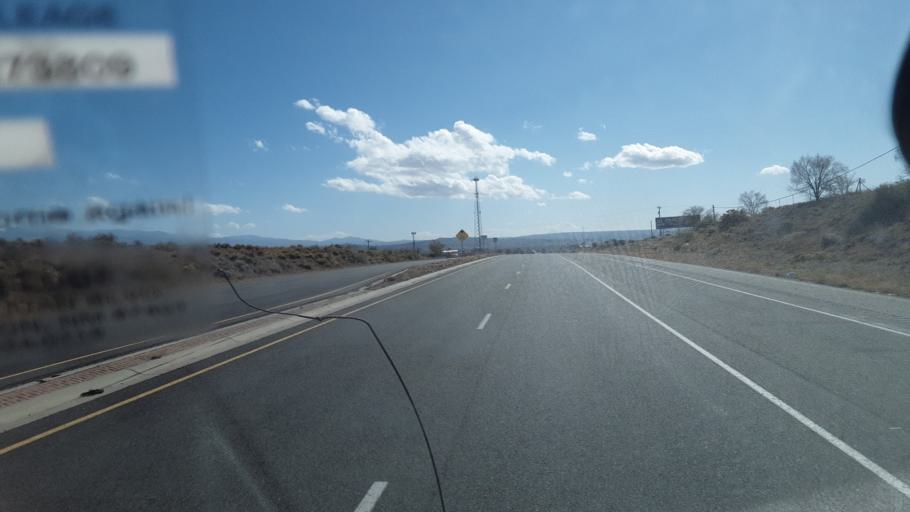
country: US
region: New Mexico
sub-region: Rio Arriba County
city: Espanola
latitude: 36.0193
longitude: -106.0908
